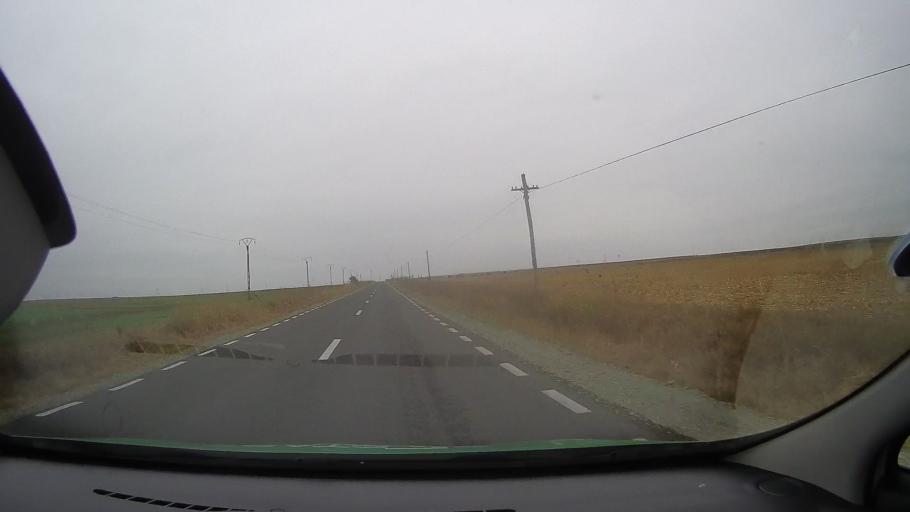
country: RO
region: Constanta
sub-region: Comuna Tortoman
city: Tortoman
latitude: 44.3527
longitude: 28.2151
